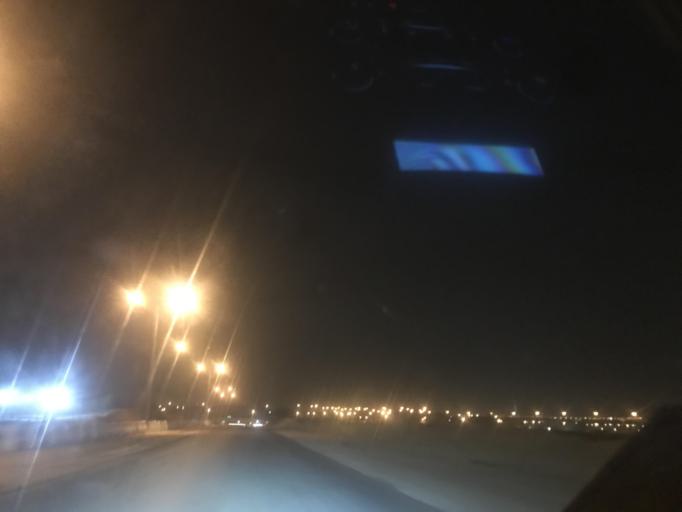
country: SA
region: Ar Riyad
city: Riyadh
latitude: 24.7602
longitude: 46.5891
